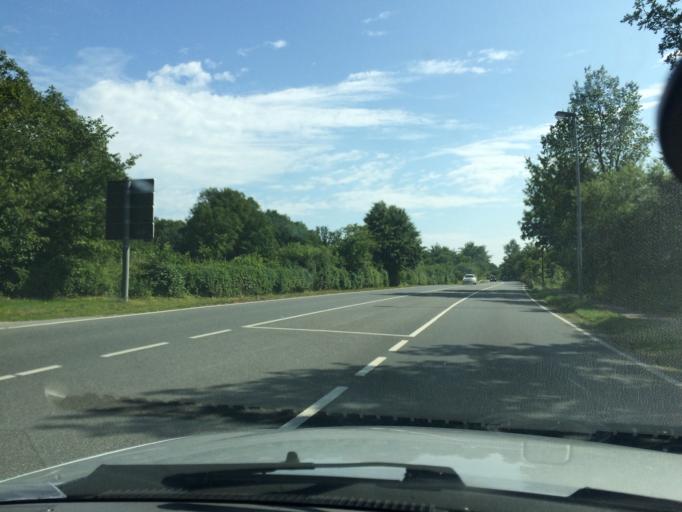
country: DE
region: Schleswig-Holstein
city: Jarplund-Weding
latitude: 54.7561
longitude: 9.4361
